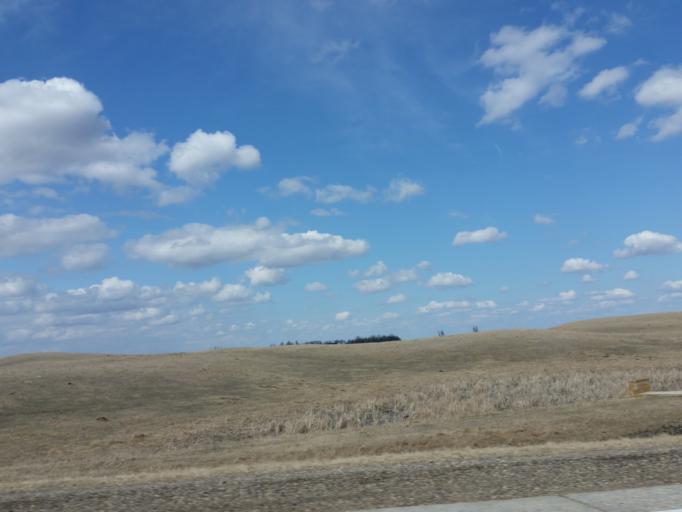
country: US
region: South Dakota
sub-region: Deuel County
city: Clear Lake
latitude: 44.8901
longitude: -96.7231
